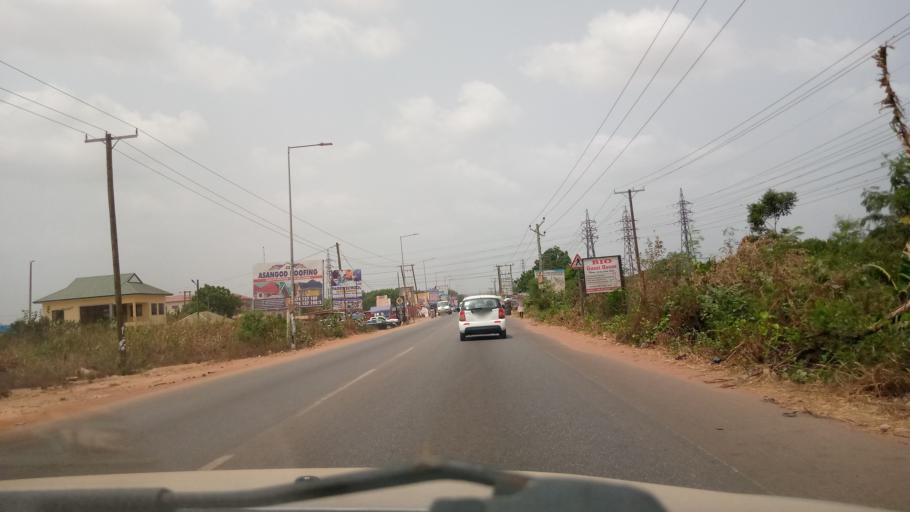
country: GH
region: Greater Accra
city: Dome
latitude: 5.6677
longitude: -0.2336
